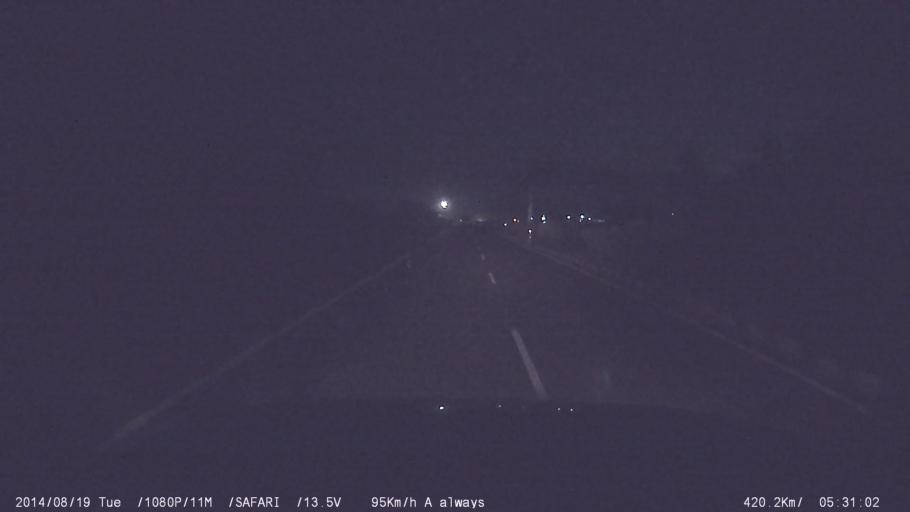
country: IN
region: Tamil Nadu
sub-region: Salem
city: Salem
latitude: 11.6186
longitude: 78.1065
